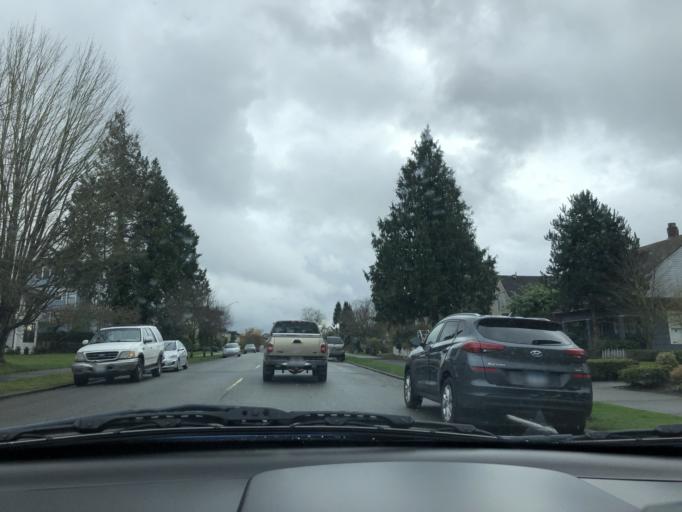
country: US
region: Washington
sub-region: Snohomish County
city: Everett
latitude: 47.9897
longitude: -122.2111
